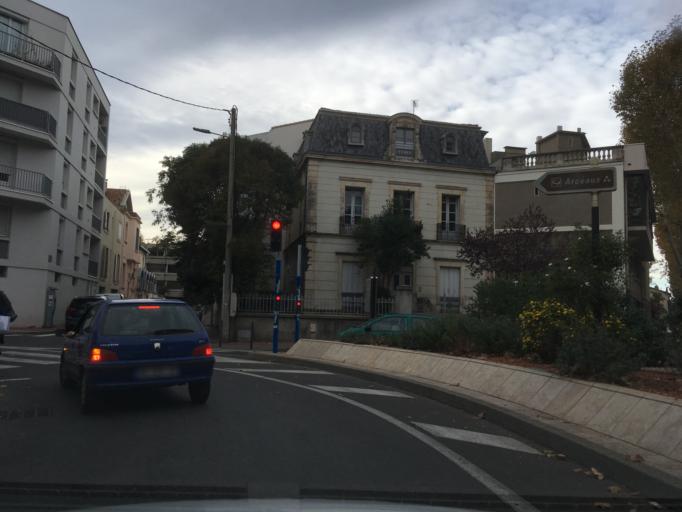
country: FR
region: Languedoc-Roussillon
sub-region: Departement de l'Herault
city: Montpellier
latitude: 43.6130
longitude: 3.8670
